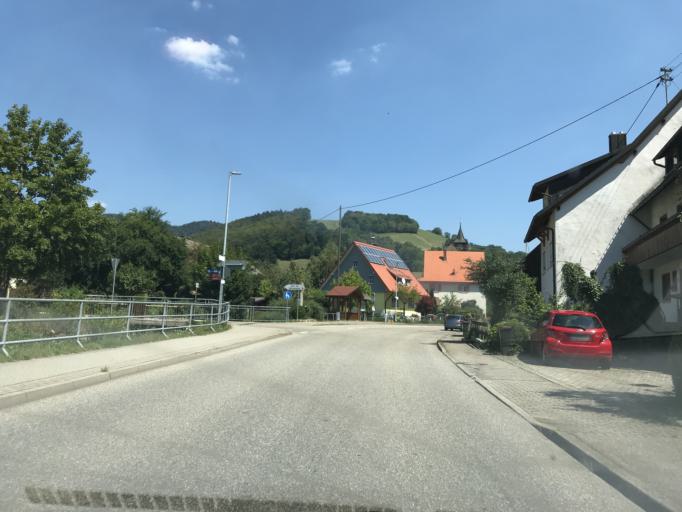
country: DE
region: Baden-Wuerttemberg
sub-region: Freiburg Region
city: Stegen
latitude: 48.0016
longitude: 7.9777
